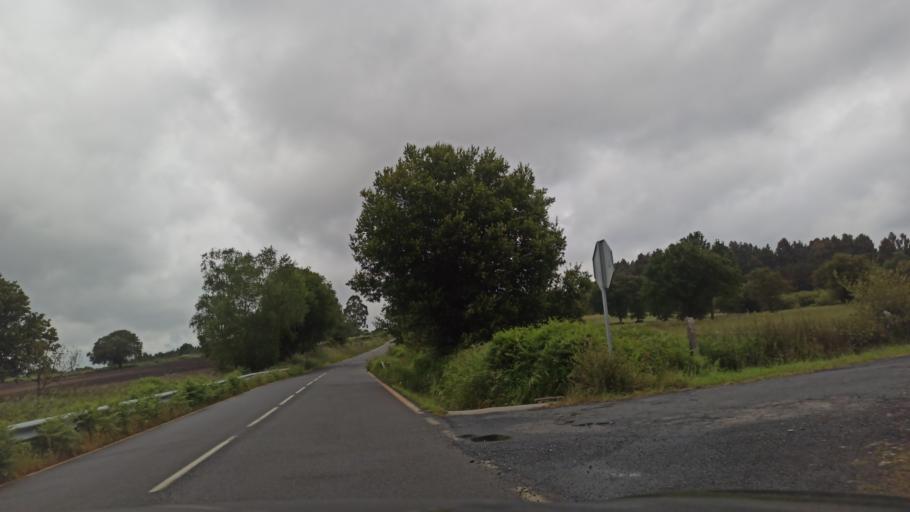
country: ES
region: Galicia
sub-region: Provincia da Coruna
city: Santiso
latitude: 42.7717
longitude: -8.0302
